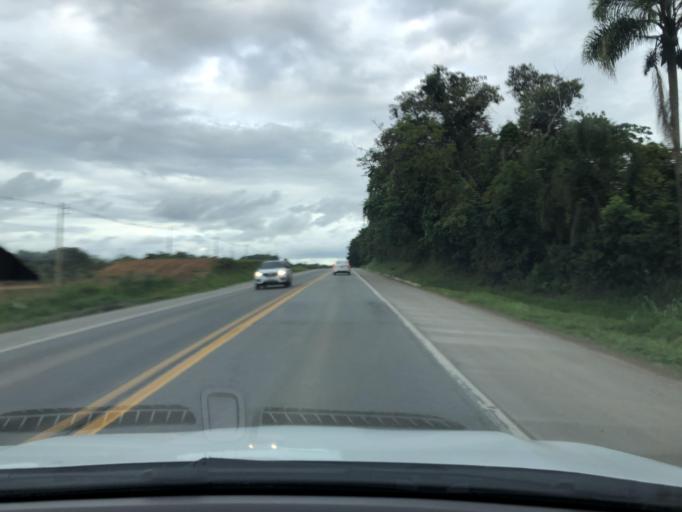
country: BR
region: Santa Catarina
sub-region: Joinville
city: Joinville
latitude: -26.4281
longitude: -48.7922
